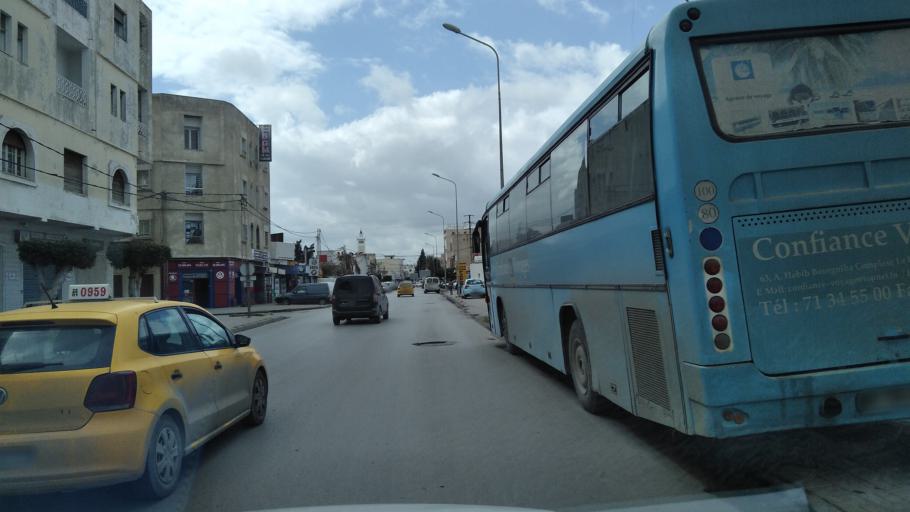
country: TN
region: Bin 'Arus
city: Ben Arous
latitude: 36.7606
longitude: 10.2239
